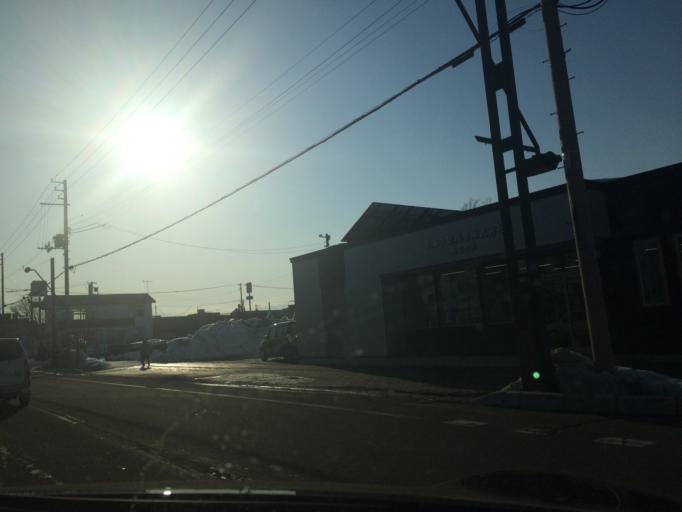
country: JP
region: Hokkaido
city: Chitose
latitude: 42.8817
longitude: 141.5853
